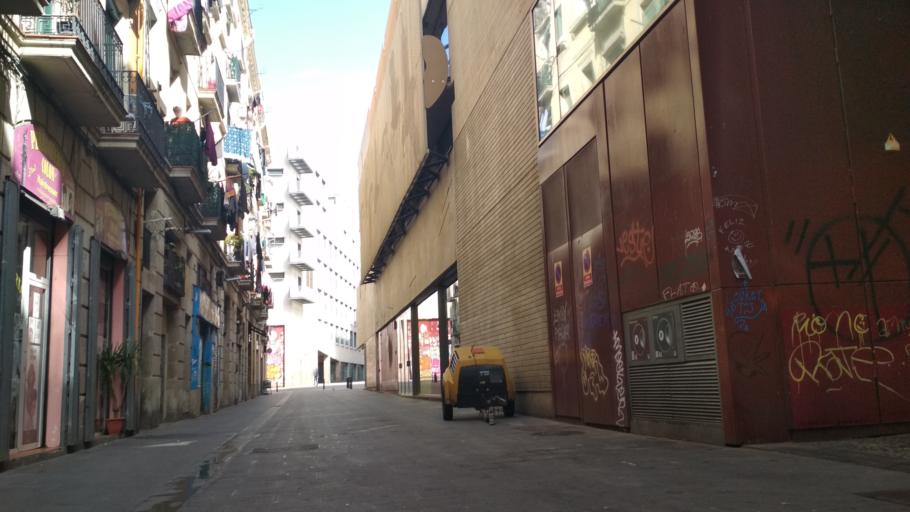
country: ES
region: Catalonia
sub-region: Provincia de Barcelona
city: Ciutat Vella
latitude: 41.3782
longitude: 2.1711
